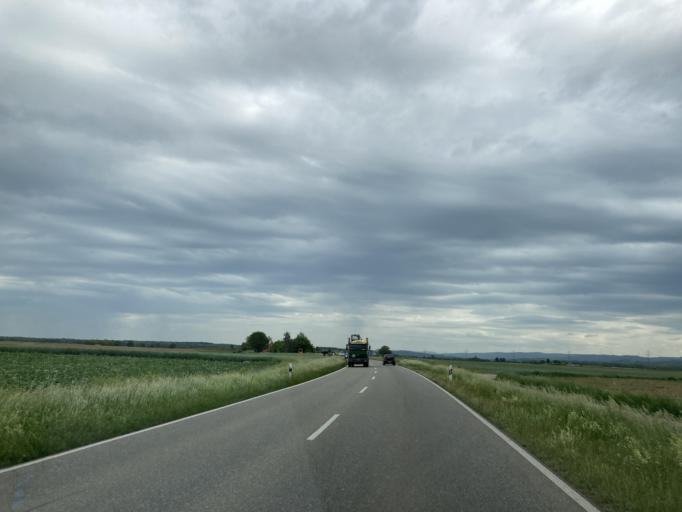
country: DE
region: Baden-Wuerttemberg
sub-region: Freiburg Region
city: Endingen
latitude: 48.1540
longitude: 7.7111
